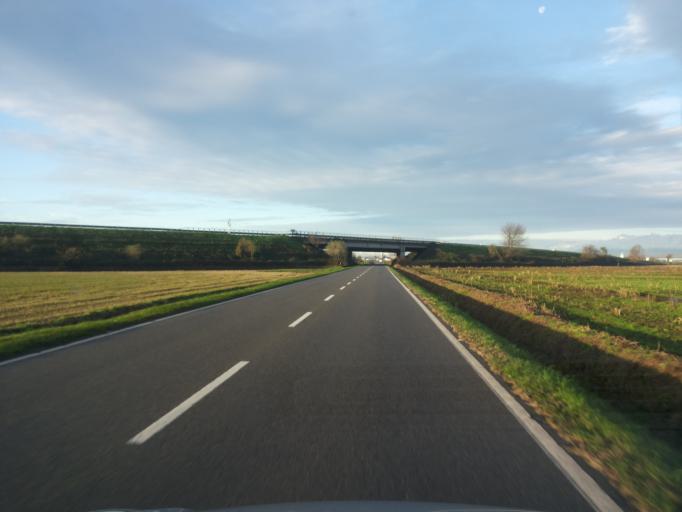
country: IT
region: Piedmont
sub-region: Provincia di Vercelli
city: Crova
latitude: 45.3448
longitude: 8.2066
